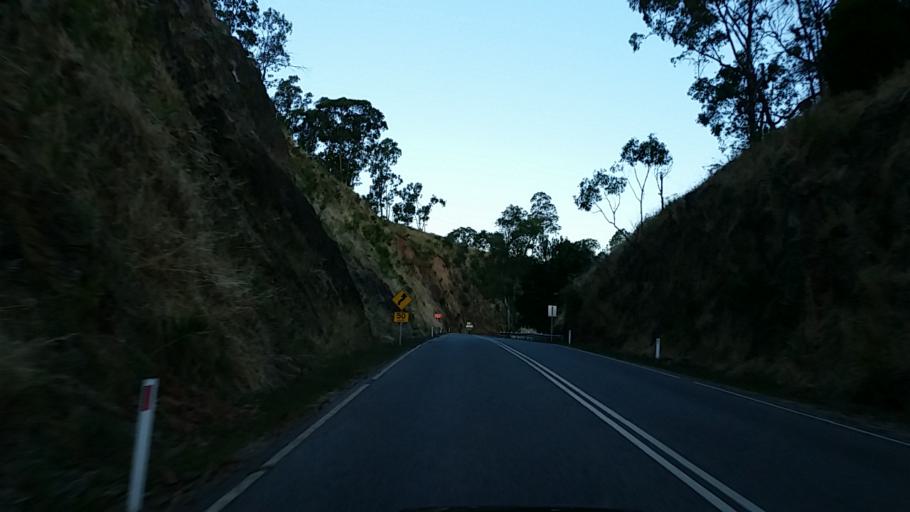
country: AU
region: South Australia
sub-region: Tea Tree Gully
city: Golden Grove
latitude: -34.8493
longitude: 138.7940
